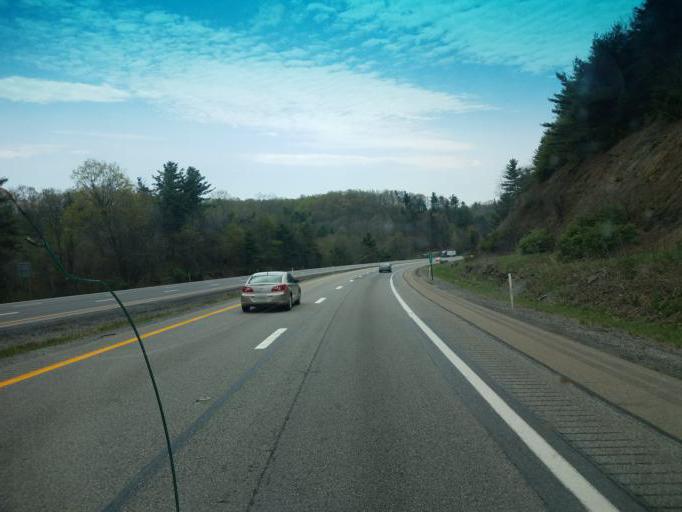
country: US
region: West Virginia
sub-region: Mercer County
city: Athens
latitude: 37.5281
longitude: -81.1091
